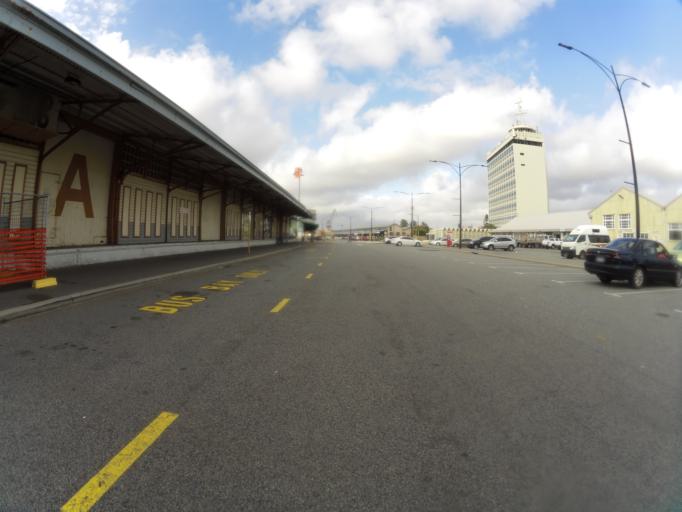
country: AU
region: Western Australia
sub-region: Fremantle
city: South Fremantle
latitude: -32.0542
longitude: 115.7401
